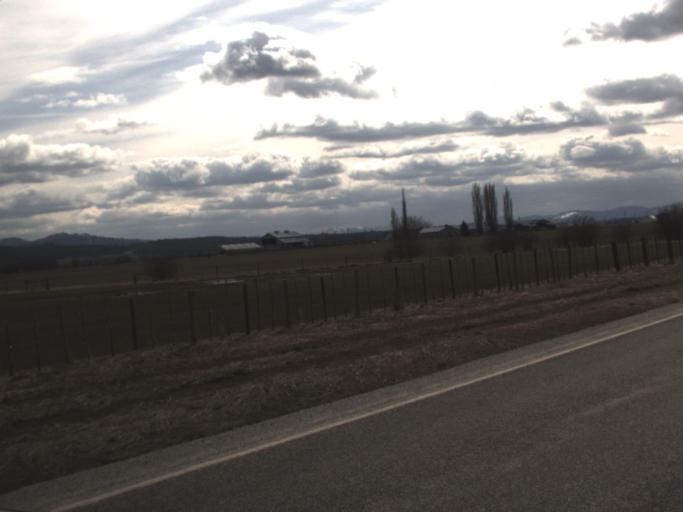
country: US
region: Washington
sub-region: Pend Oreille County
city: Newport
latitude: 48.3648
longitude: -117.3047
